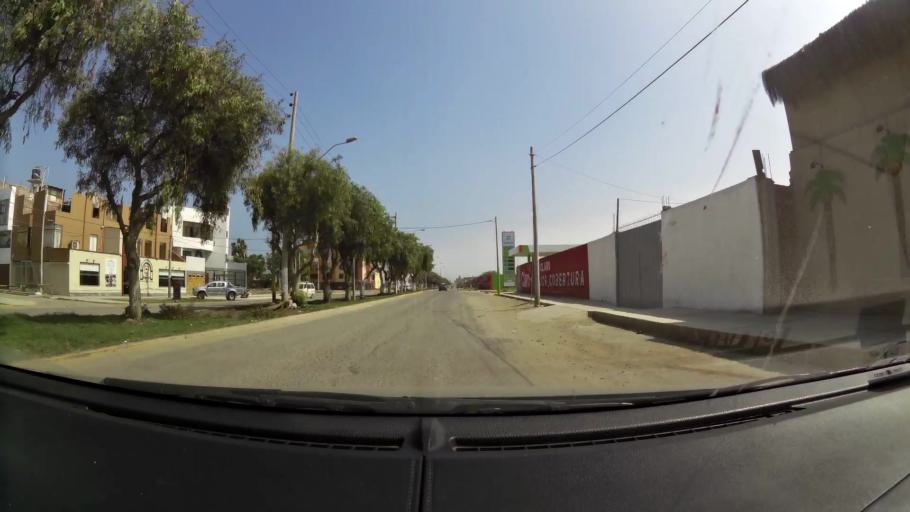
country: PE
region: La Libertad
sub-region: Provincia de Trujillo
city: Buenos Aires
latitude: -8.1273
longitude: -79.0473
